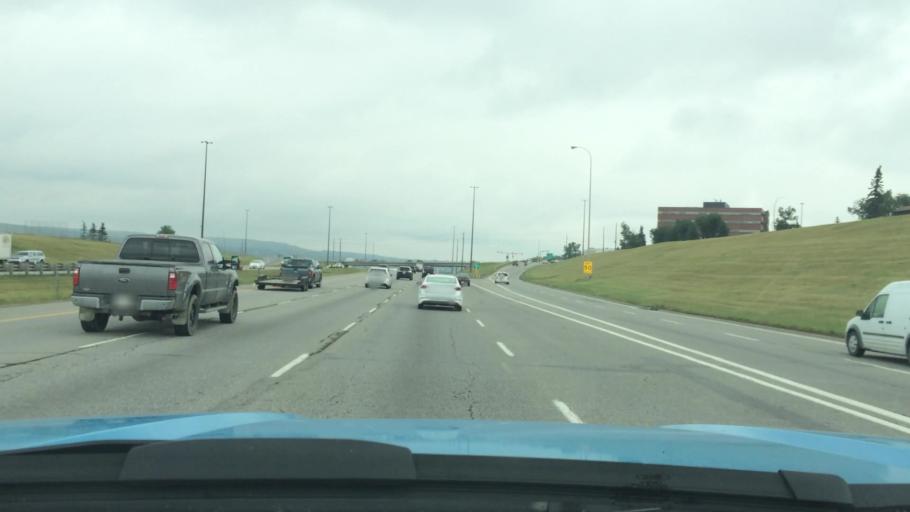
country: CA
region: Alberta
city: Calgary
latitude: 51.0778
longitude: -114.0297
